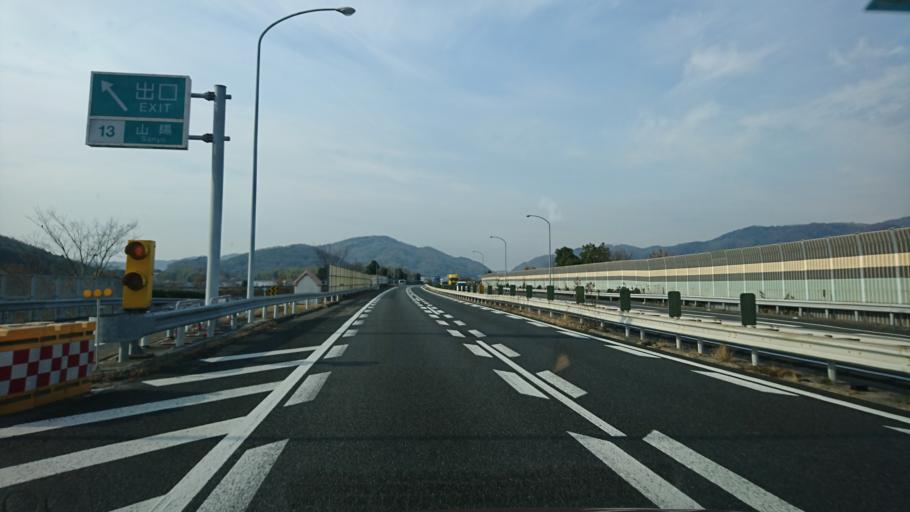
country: JP
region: Okayama
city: Okayama-shi
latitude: 34.7438
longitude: 134.0258
